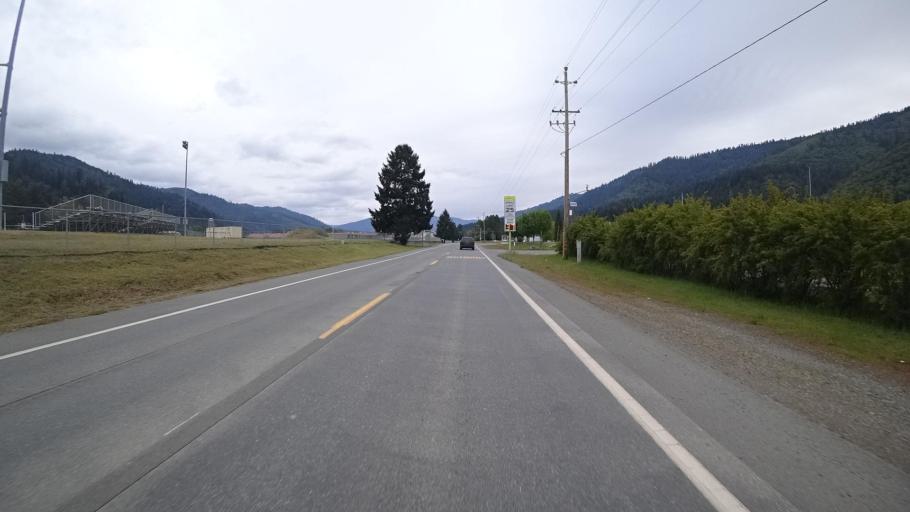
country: US
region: California
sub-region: Humboldt County
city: Willow Creek
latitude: 41.0466
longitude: -123.6732
